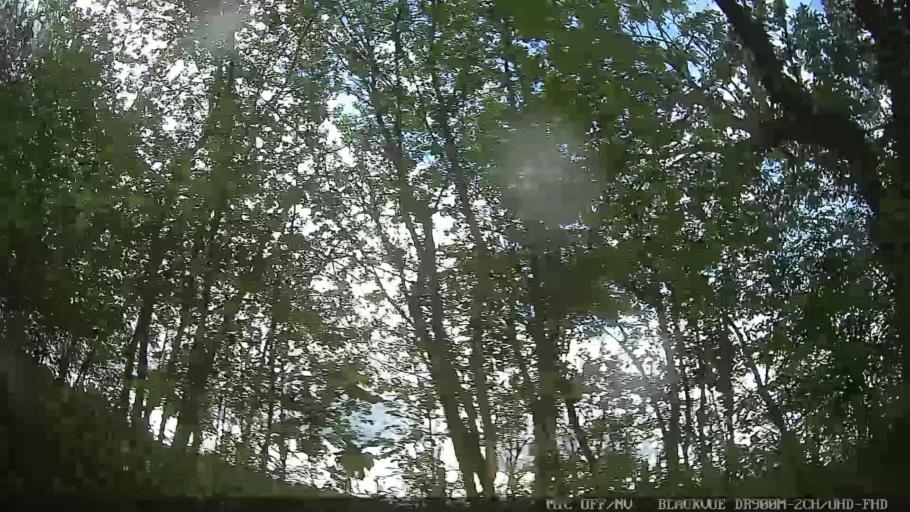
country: BR
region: Sao Paulo
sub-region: Jaguariuna
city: Jaguariuna
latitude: -22.6610
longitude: -47.0495
